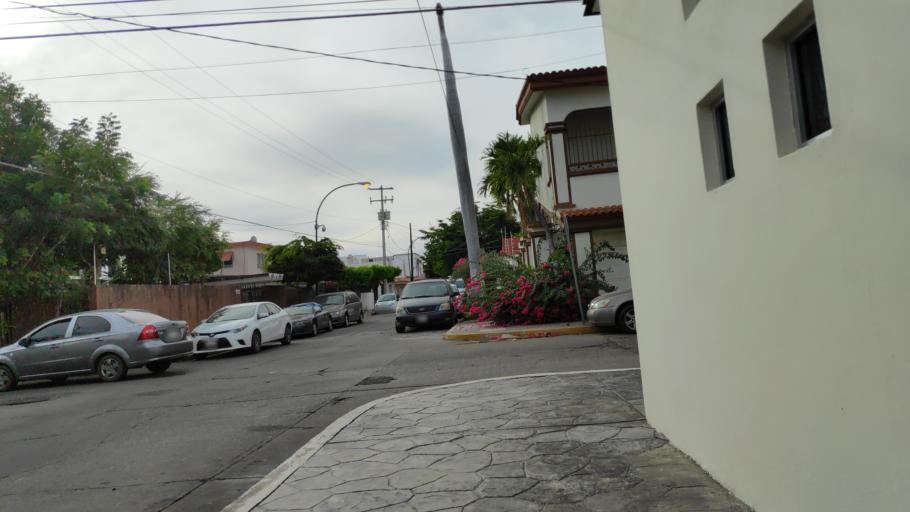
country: MX
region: Sinaloa
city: Culiacan
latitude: 24.7943
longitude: -107.3948
